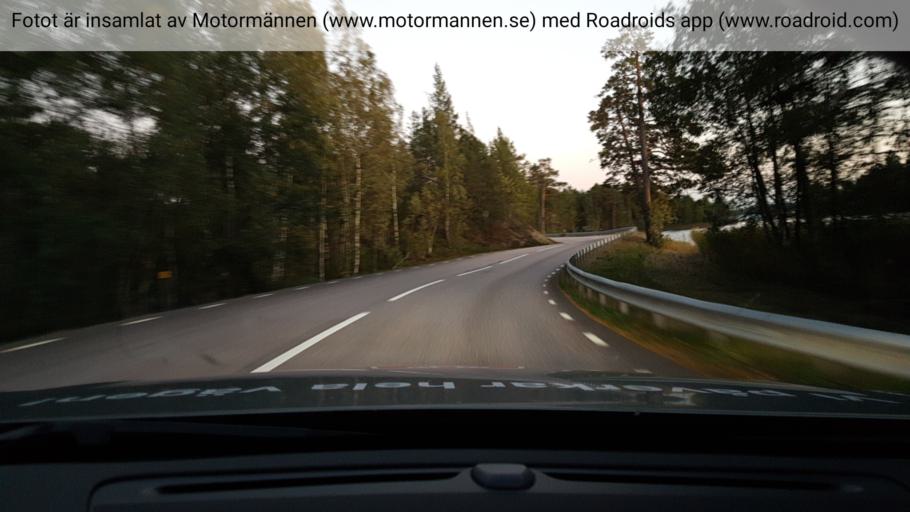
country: SE
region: OErebro
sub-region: Laxa Kommun
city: Laxa
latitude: 58.9080
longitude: 14.7153
